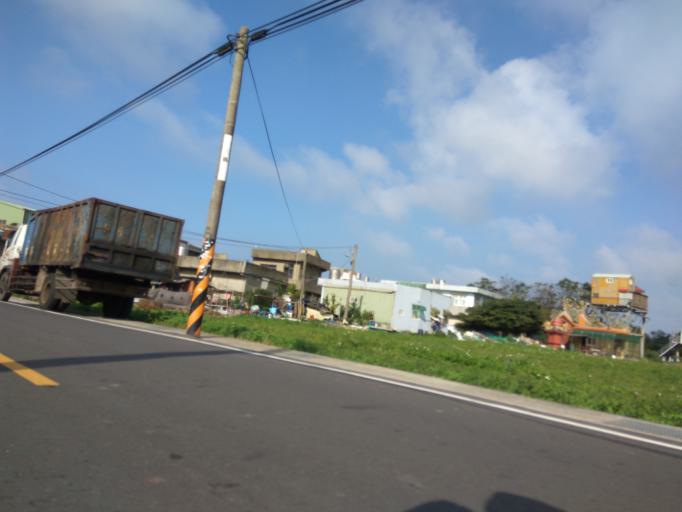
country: TW
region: Taiwan
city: Taoyuan City
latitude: 25.0634
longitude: 121.1730
